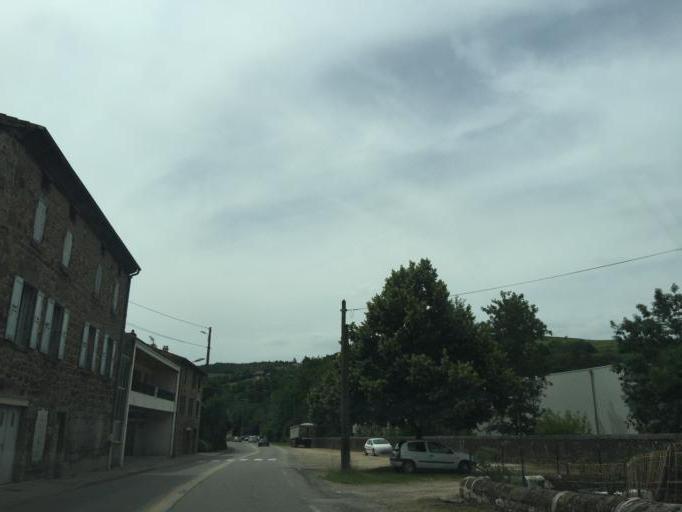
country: FR
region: Rhone-Alpes
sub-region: Departement de l'Ardeche
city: Saint-Marcel-les-Annonay
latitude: 45.2870
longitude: 4.6307
